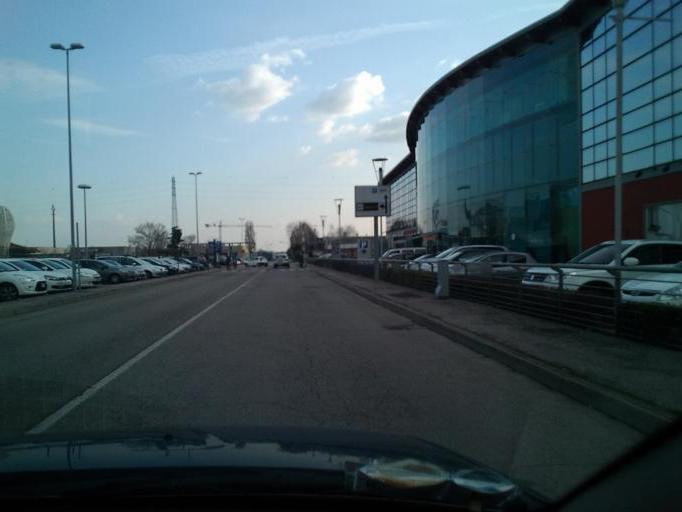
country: IT
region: Veneto
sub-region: Provincia di Verona
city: Lugagnano
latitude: 45.4403
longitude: 10.8619
